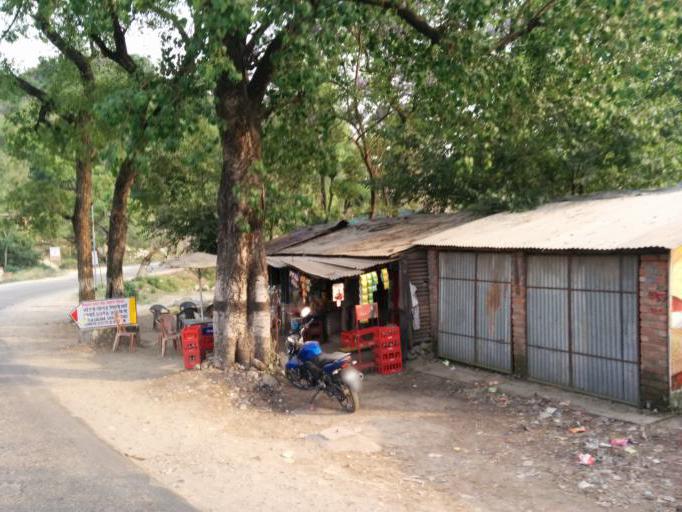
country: IN
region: Himachal Pradesh
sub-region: Kangra
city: Kotla
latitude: 32.2372
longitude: 76.0476
